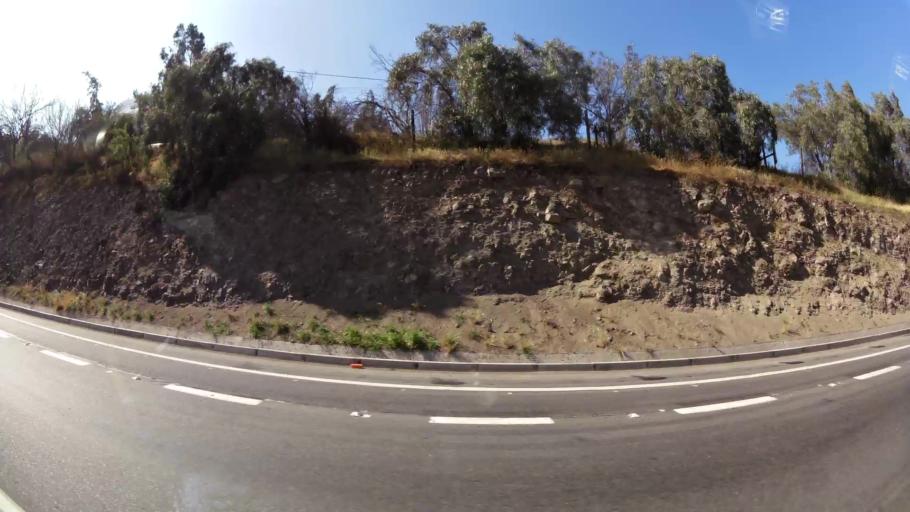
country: CL
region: Santiago Metropolitan
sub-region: Provincia de Chacabuco
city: Chicureo Abajo
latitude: -33.3147
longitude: -70.7042
